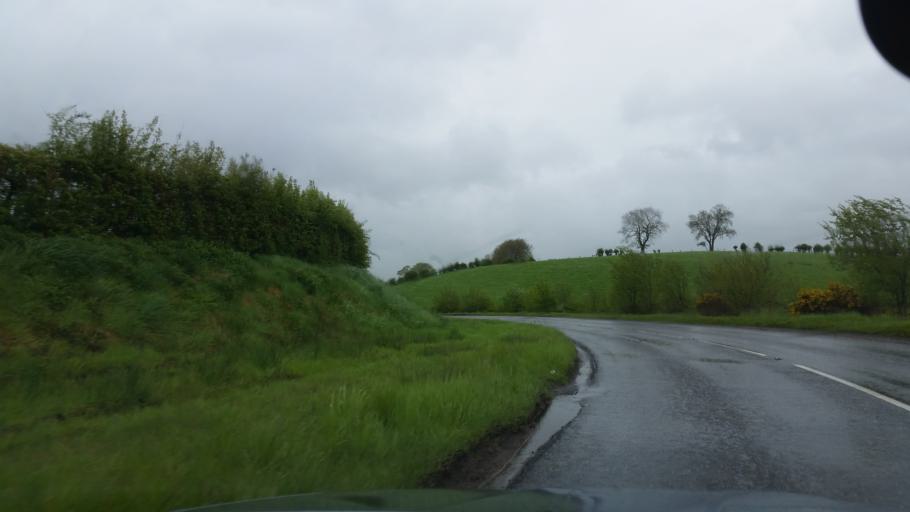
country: GB
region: Northern Ireland
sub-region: Omagh District
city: Omagh
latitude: 54.5707
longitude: -7.2763
